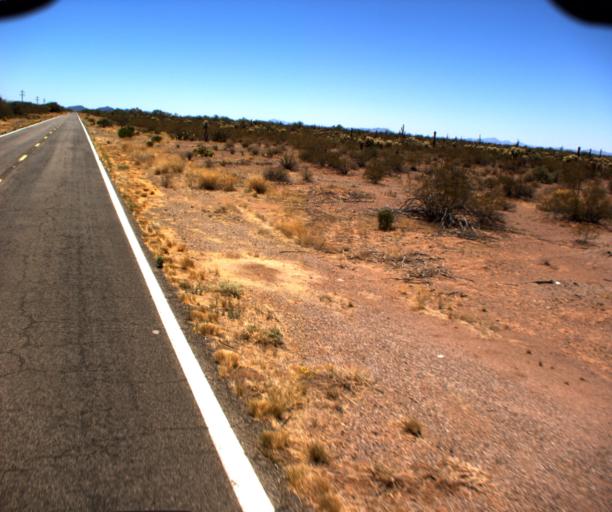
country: US
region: Arizona
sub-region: Pima County
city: Sells
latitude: 32.0736
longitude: -112.0443
